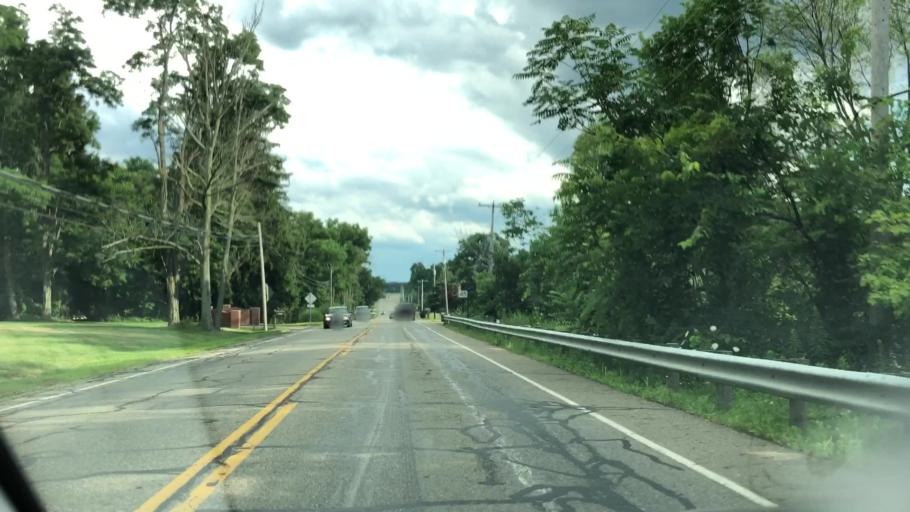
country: US
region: Ohio
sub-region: Summit County
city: Greensburg
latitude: 40.9207
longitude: -81.4629
